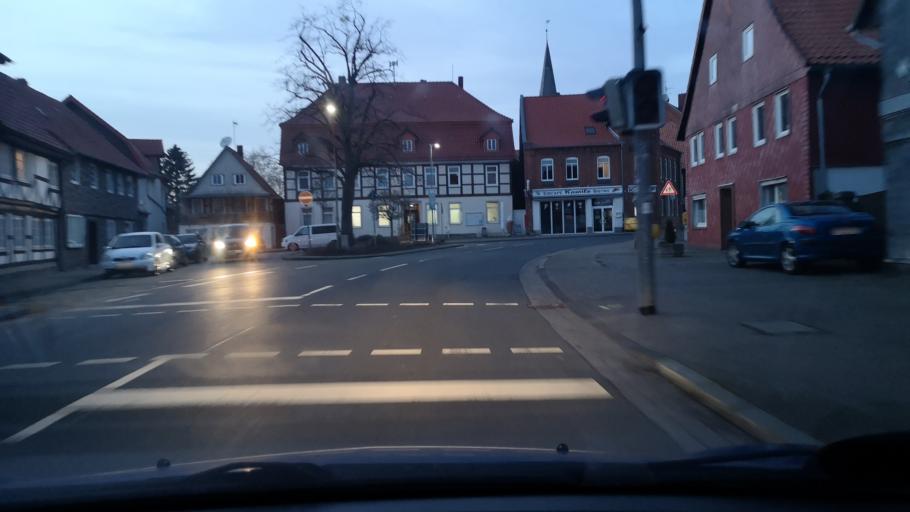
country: DE
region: Lower Saxony
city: Coppenbrugge
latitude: 52.1193
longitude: 9.5484
